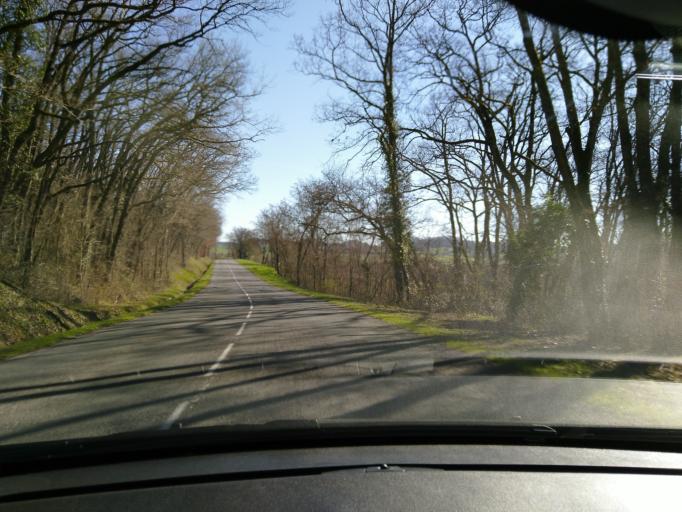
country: FR
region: Aquitaine
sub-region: Departement du Lot-et-Garonne
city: Cancon
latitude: 44.5343
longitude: 0.6501
